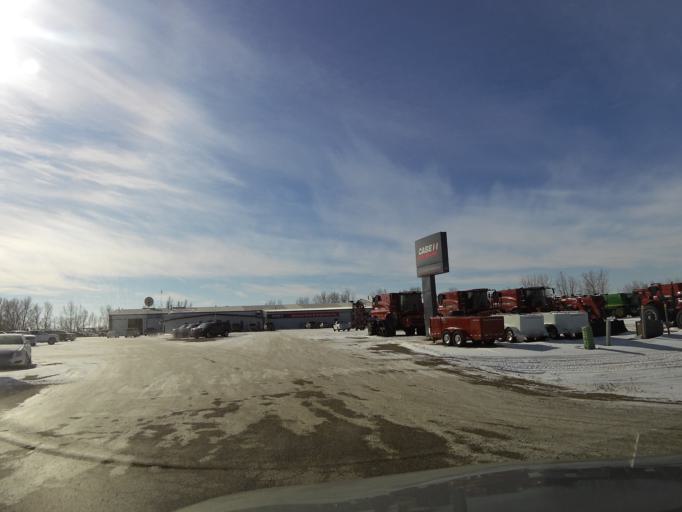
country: US
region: North Dakota
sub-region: Walsh County
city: Grafton
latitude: 48.4125
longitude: -97.4415
